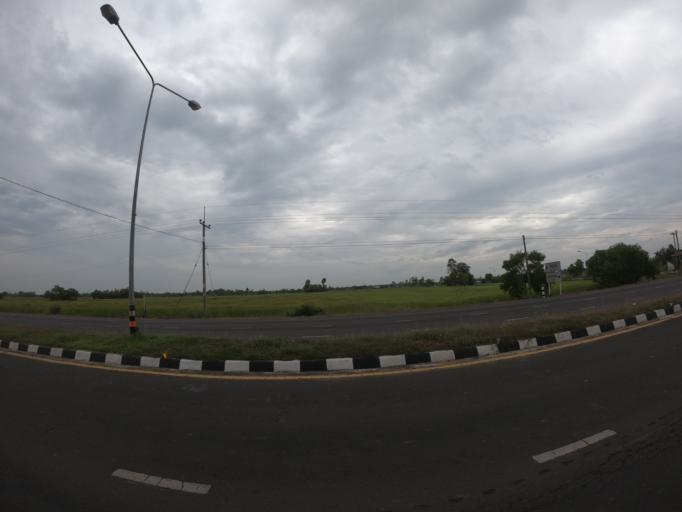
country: TH
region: Roi Et
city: Thawat Buri
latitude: 16.0924
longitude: 103.7805
